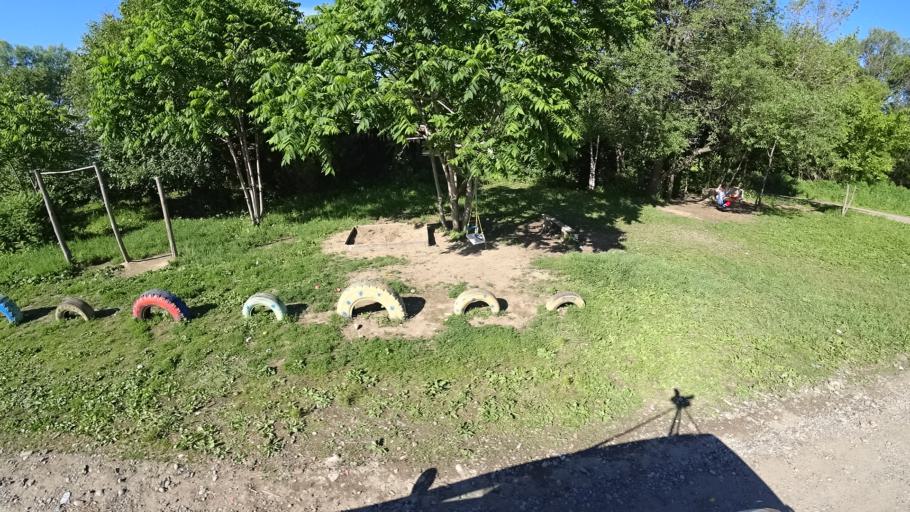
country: RU
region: Khabarovsk Krai
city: Khor
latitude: 47.8895
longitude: 134.9937
